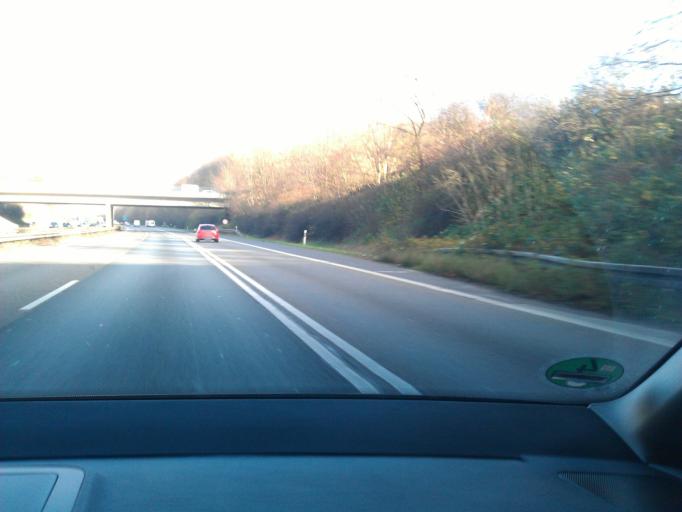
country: DE
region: North Rhine-Westphalia
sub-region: Regierungsbezirk Koln
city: Mengenich
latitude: 51.0002
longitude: 6.8992
